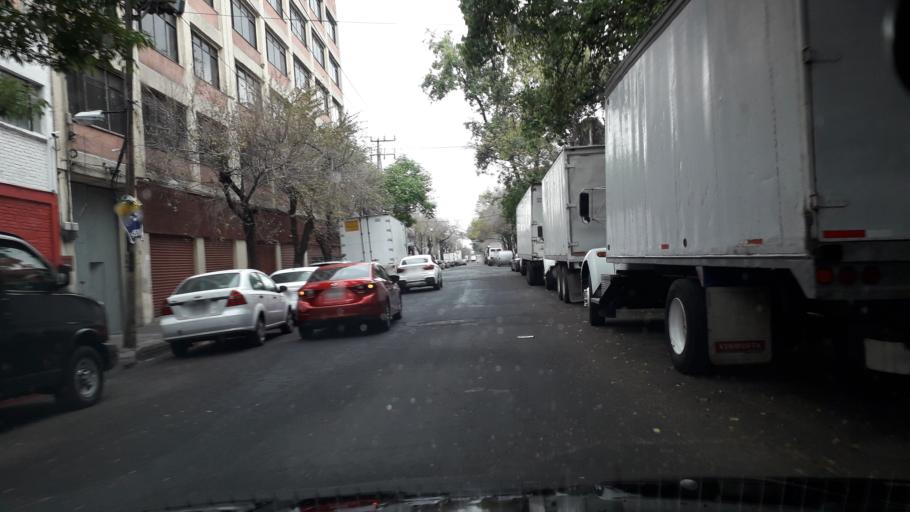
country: MX
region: Mexico City
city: Cuauhtemoc
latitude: 19.4599
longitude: -99.1488
